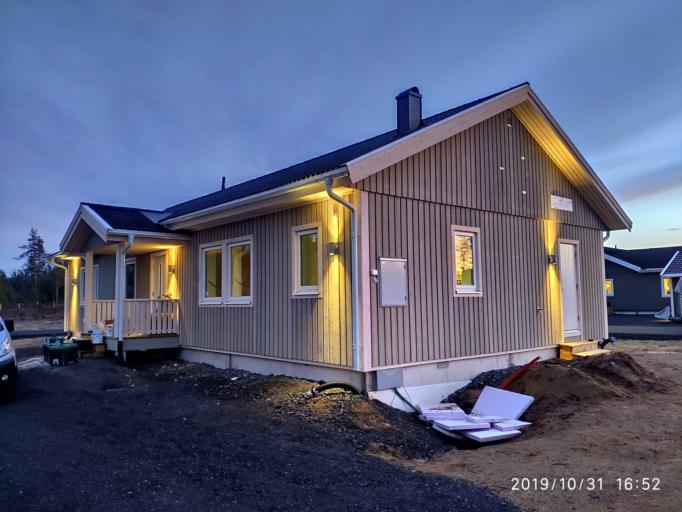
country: NO
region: Buskerud
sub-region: Modum
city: Vikersund
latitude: 60.2527
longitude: 9.9341
